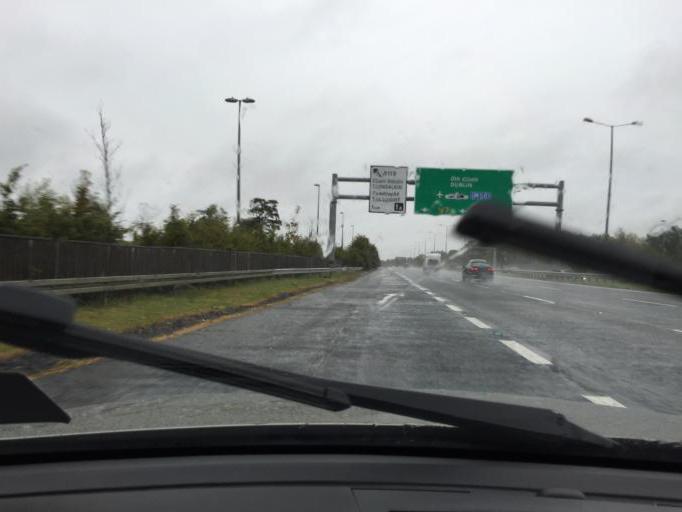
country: IE
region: Leinster
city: Clondalkin
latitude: 53.3043
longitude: -6.4139
